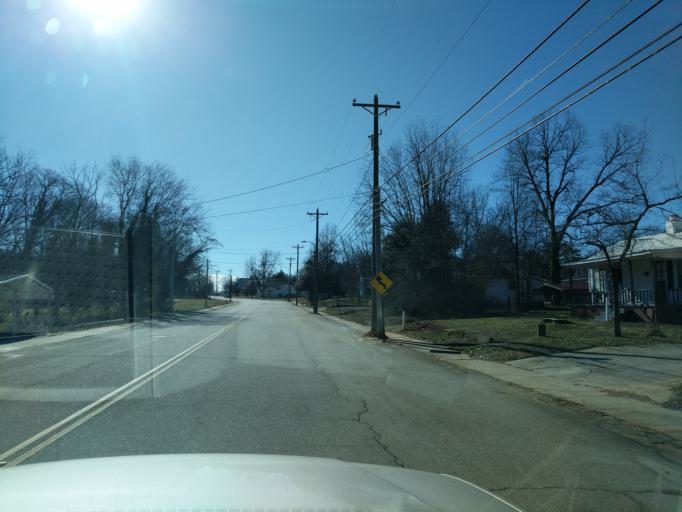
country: US
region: South Carolina
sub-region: Laurens County
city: Clinton
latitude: 34.4846
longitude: -81.8818
